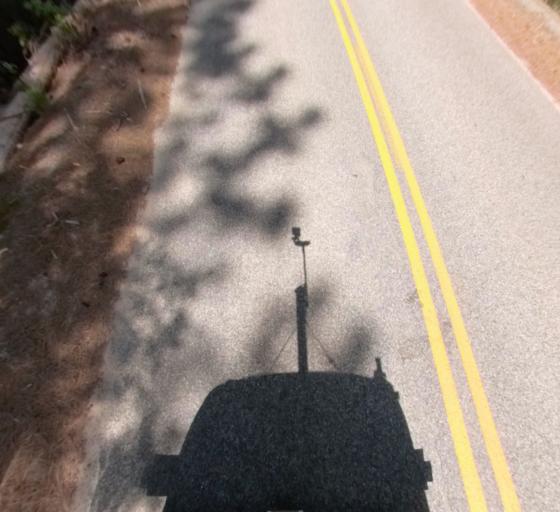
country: US
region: California
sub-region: Madera County
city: Oakhurst
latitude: 37.3815
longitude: -119.3950
